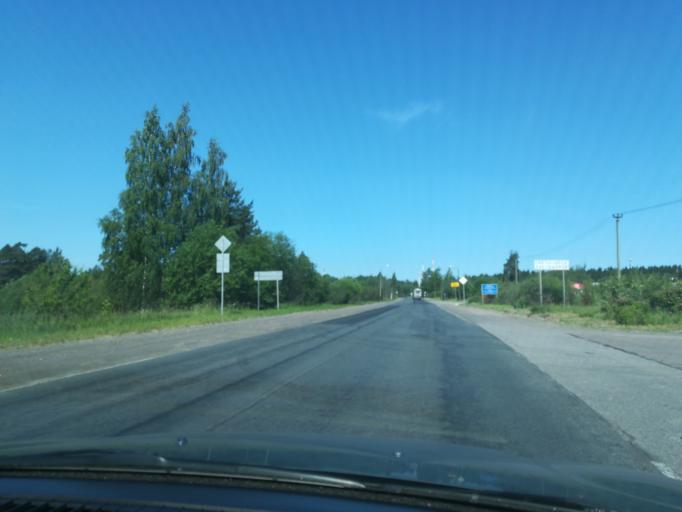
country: RU
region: Leningrad
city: Svetogorsk
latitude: 61.0935
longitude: 28.8910
